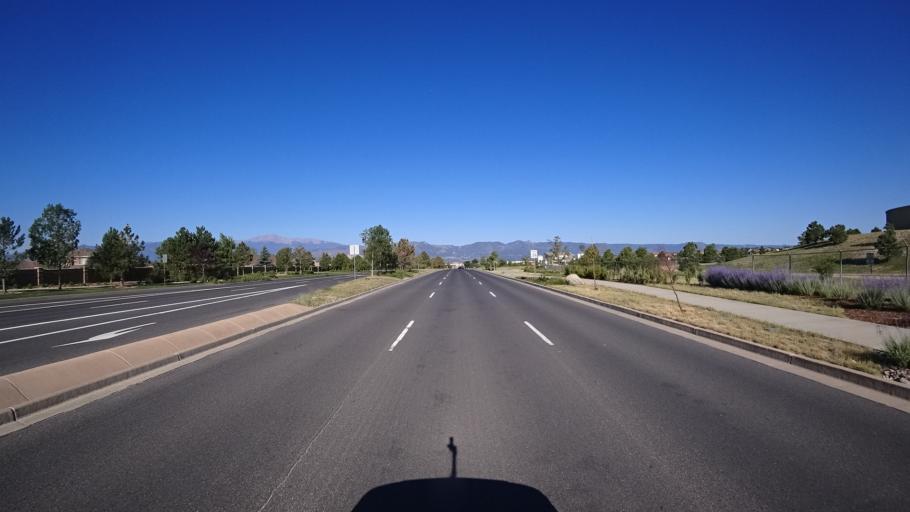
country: US
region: Colorado
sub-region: El Paso County
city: Black Forest
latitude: 38.9712
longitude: -104.7327
